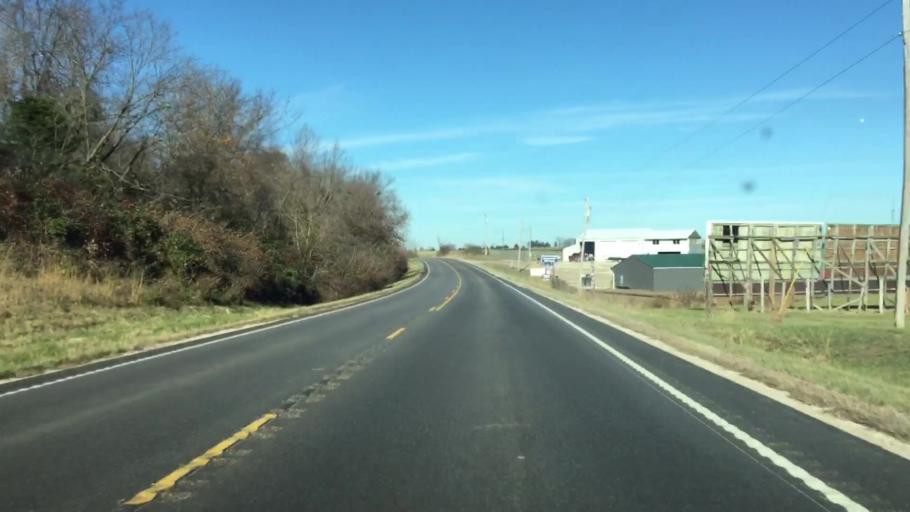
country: US
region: Missouri
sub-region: Miller County
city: Eldon
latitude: 38.3528
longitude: -92.5961
